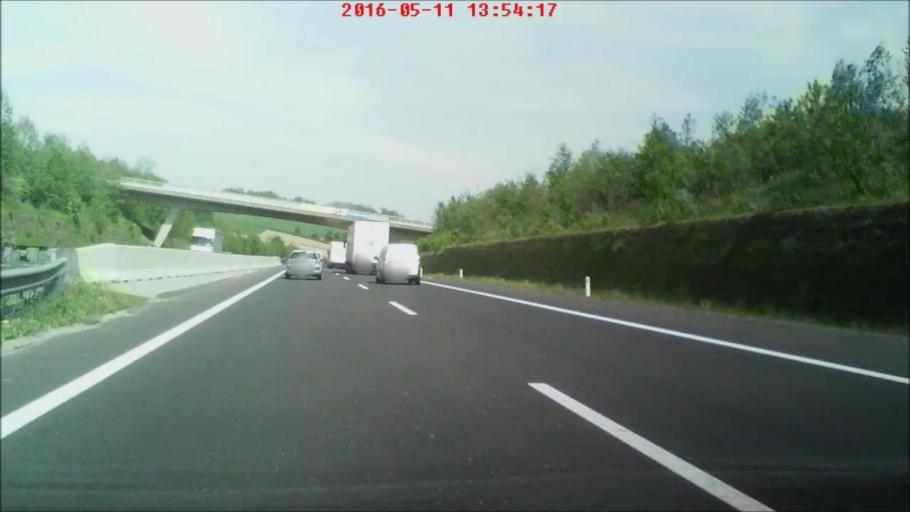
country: AT
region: Upper Austria
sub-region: Wels-Land
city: Offenhausen
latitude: 48.1821
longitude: 13.8085
